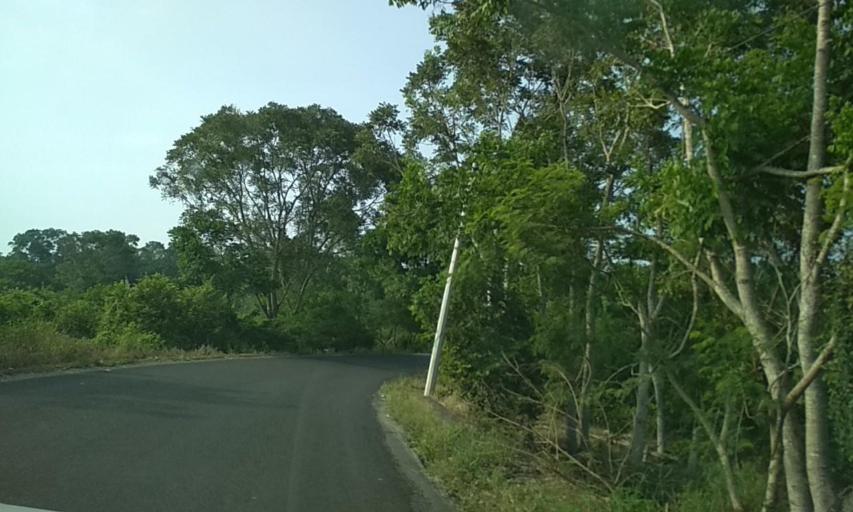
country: MX
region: Veracruz
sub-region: Misantla
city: La Defensa
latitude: 20.0498
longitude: -96.9797
